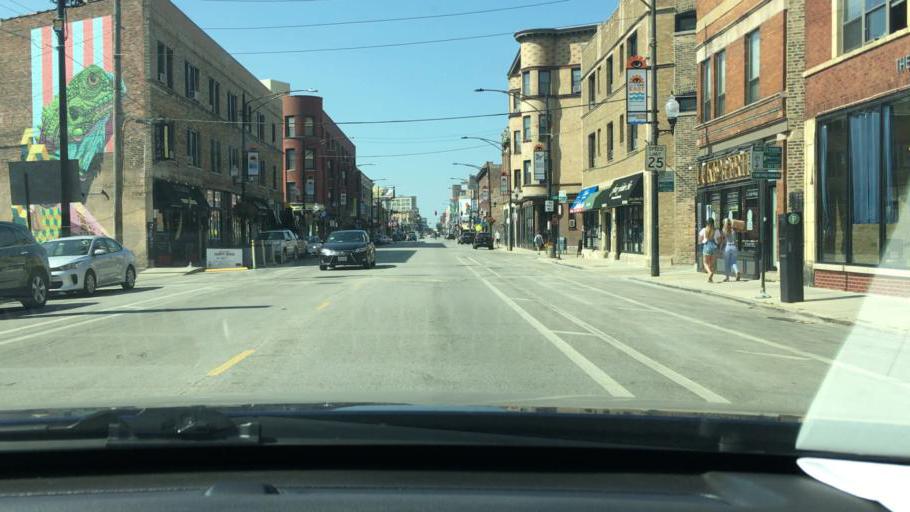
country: US
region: Illinois
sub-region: Cook County
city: Chicago
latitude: 41.9351
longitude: -87.6467
